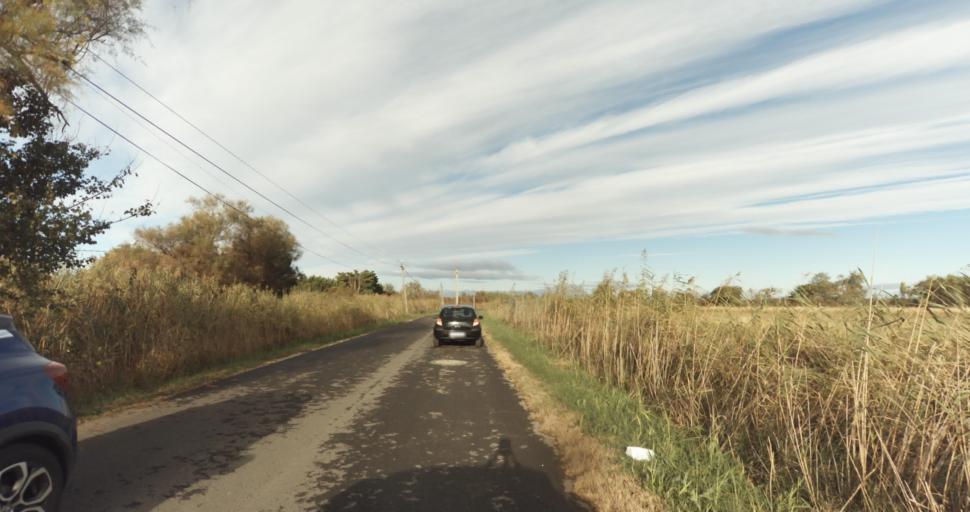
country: FR
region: Languedoc-Roussillon
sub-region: Departement du Gard
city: Aigues-Mortes
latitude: 43.5613
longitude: 4.2146
